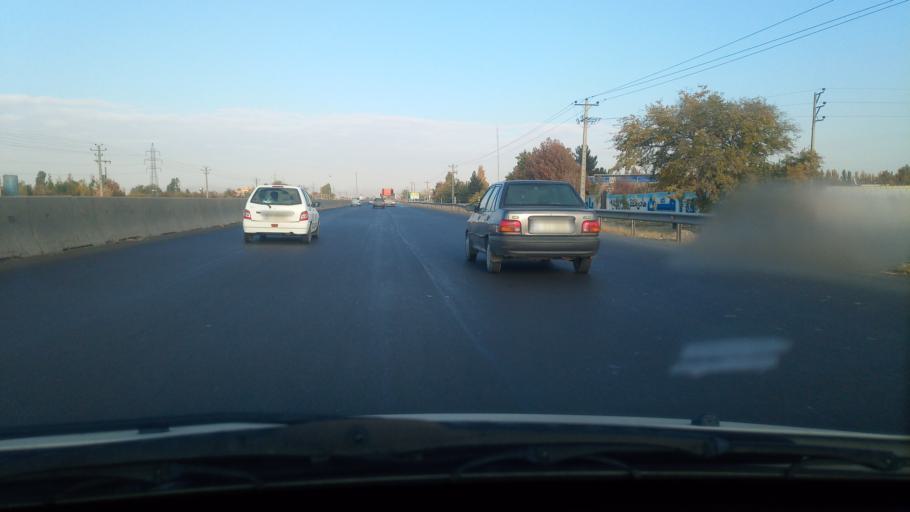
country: IR
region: Razavi Khorasan
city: Chenaran
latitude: 36.5476
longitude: 59.2665
